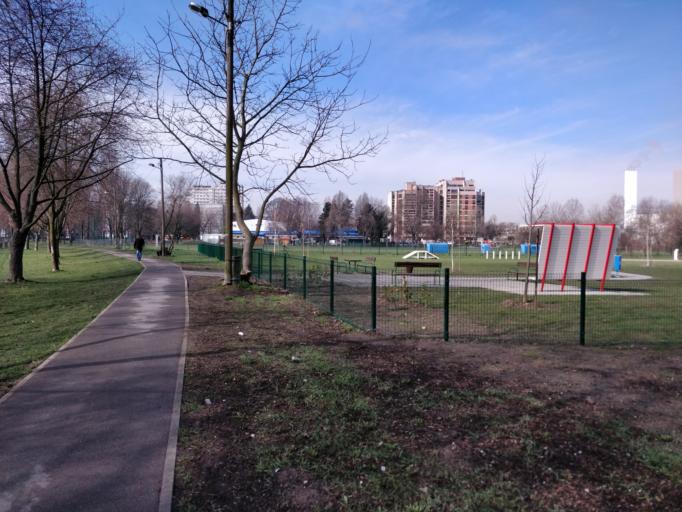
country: HR
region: Grad Zagreb
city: Novi Zagreb
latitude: 45.7940
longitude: 16.0122
